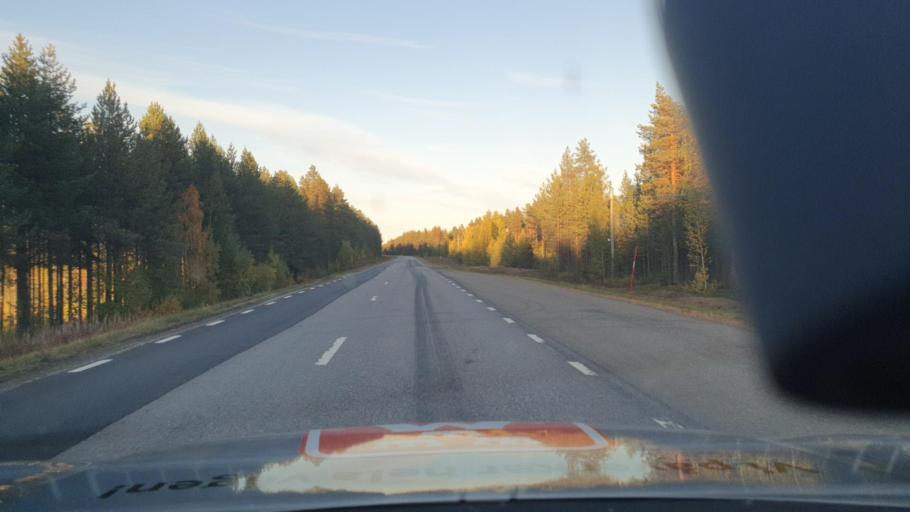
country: SE
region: Norrbotten
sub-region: Pajala Kommun
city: Pajala
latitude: 67.2418
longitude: 23.1165
